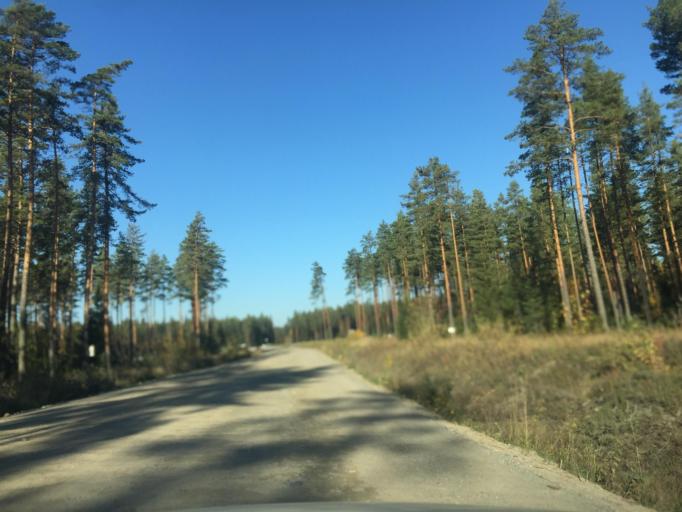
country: RU
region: Republic of Karelia
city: Lakhdenpokh'ya
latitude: 61.3846
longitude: 29.9626
